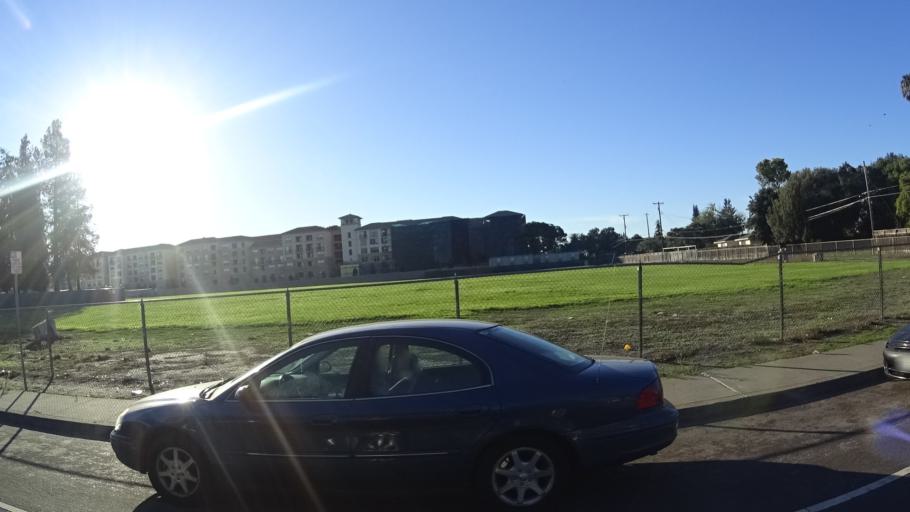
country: US
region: California
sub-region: Santa Clara County
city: Santa Clara
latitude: 37.3686
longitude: -121.9904
